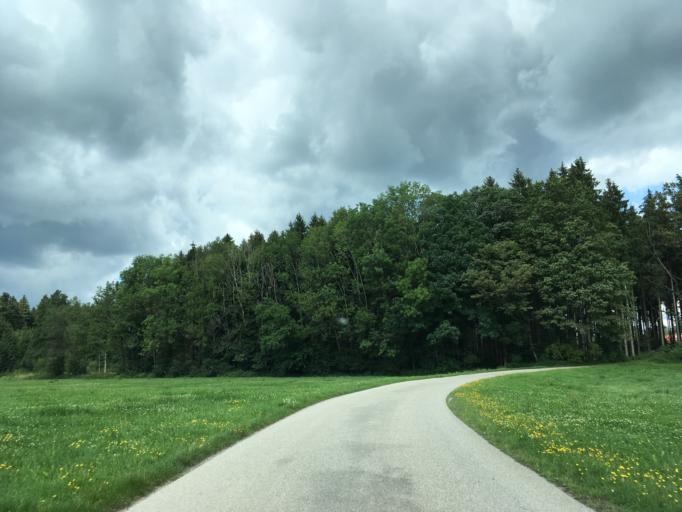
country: DE
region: Bavaria
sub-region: Upper Bavaria
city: Pittenhart
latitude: 48.0092
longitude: 12.3663
